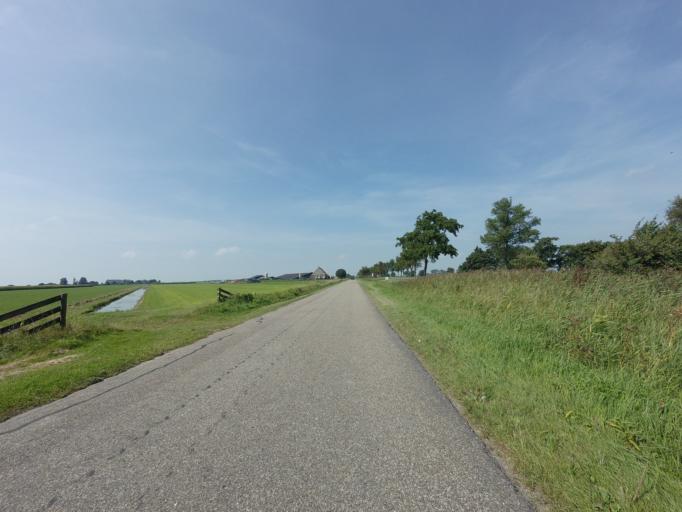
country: NL
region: Friesland
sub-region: Sudwest Fryslan
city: Woudsend
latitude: 52.9317
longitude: 5.6656
